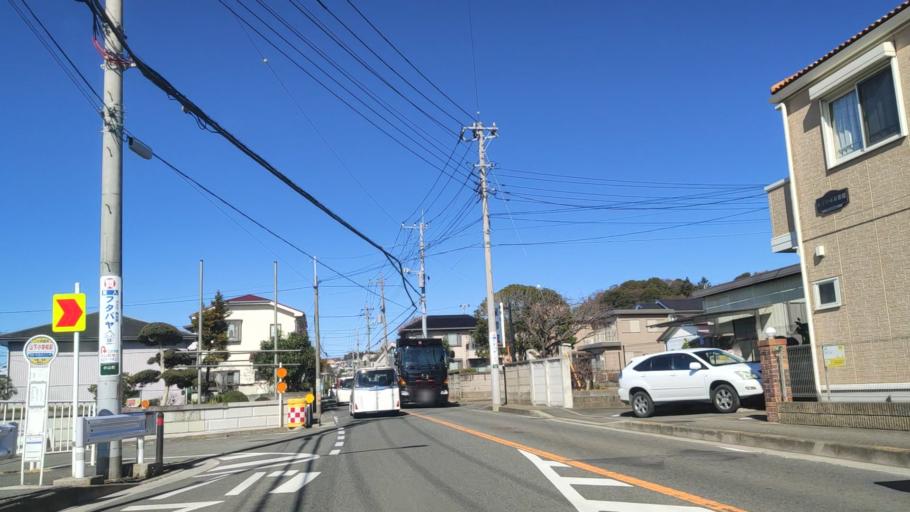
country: JP
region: Tokyo
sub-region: Machida-shi
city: Machida
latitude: 35.5221
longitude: 139.5348
